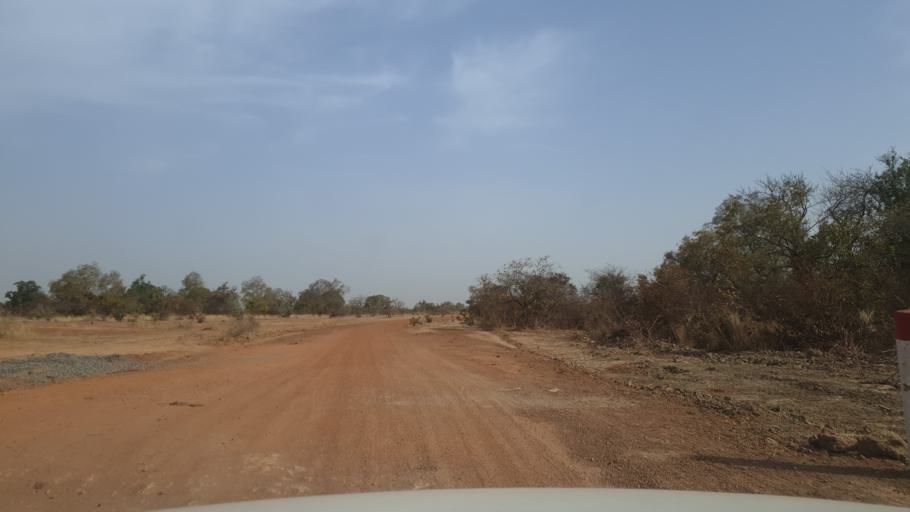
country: ML
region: Koulikoro
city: Kolokani
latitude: 13.3103
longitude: -8.2792
